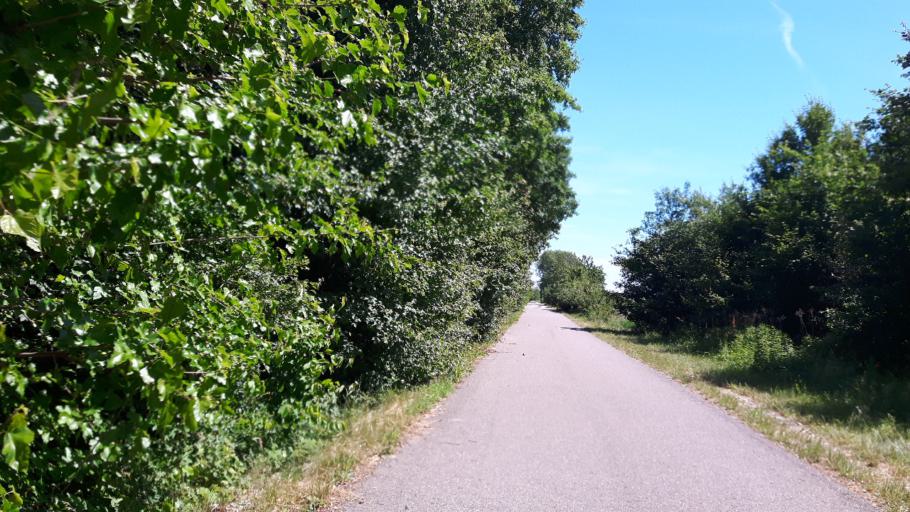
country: DE
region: Saxony-Anhalt
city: Lutzen
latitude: 51.2509
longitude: 12.1776
